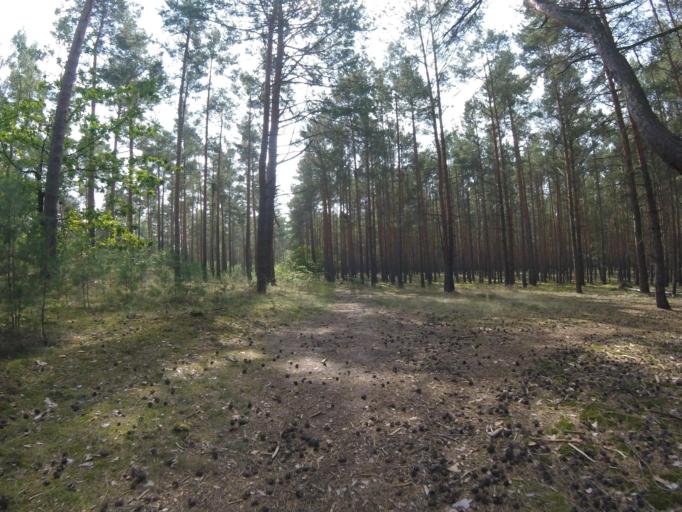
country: DE
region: Brandenburg
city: Bestensee
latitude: 52.2727
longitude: 13.6628
